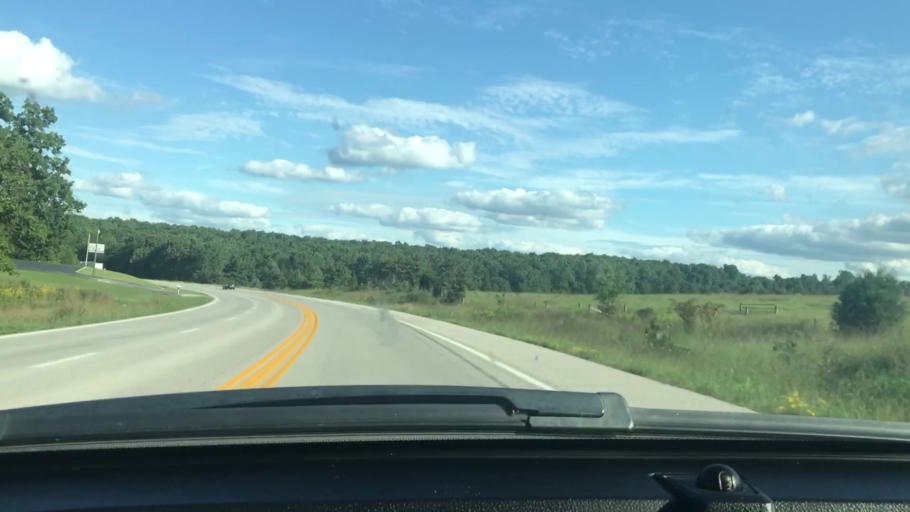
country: US
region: Missouri
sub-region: Howell County
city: West Plains
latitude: 36.6619
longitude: -91.7214
